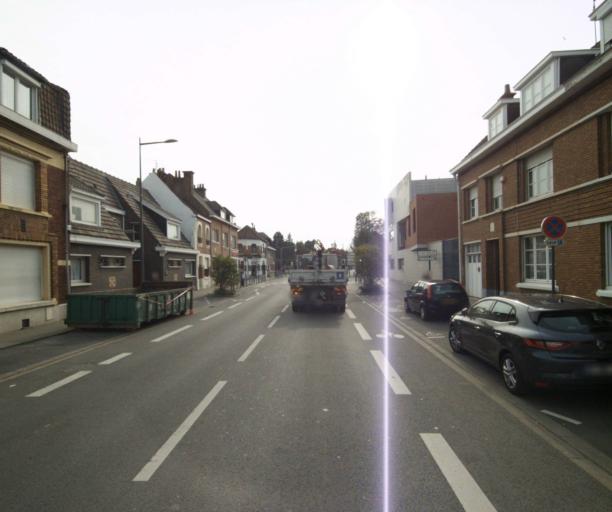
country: FR
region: Nord-Pas-de-Calais
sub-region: Departement du Nord
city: Seclin
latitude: 50.5474
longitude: 3.0274
